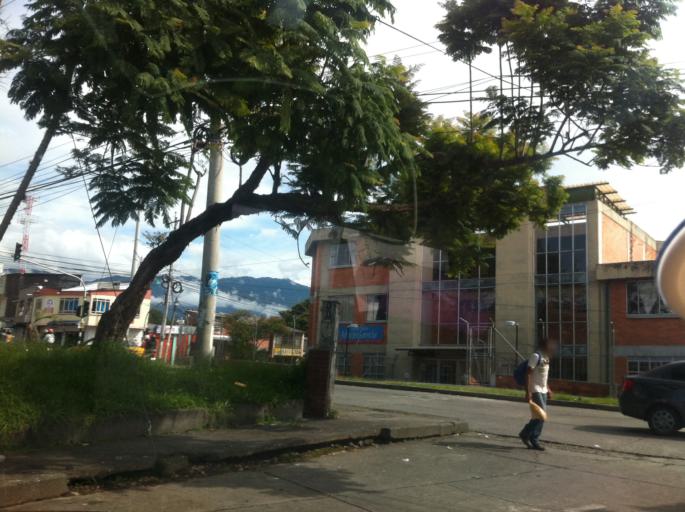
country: CO
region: Quindio
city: Armenia
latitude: 4.5235
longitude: -75.6931
